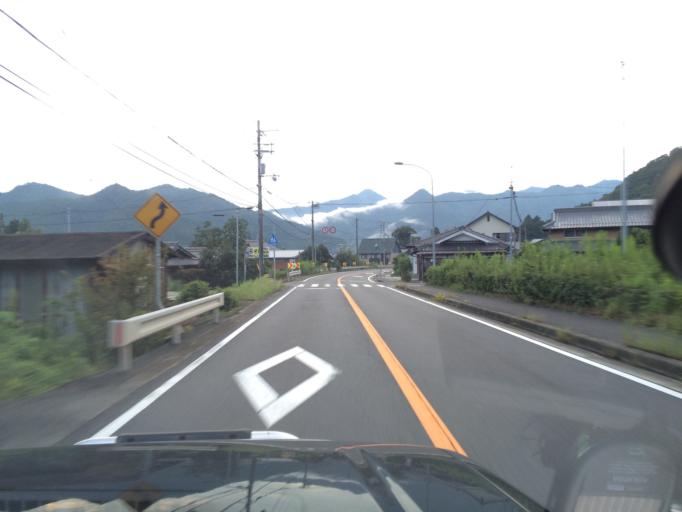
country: JP
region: Hyogo
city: Nishiwaki
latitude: 35.0919
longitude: 134.9990
